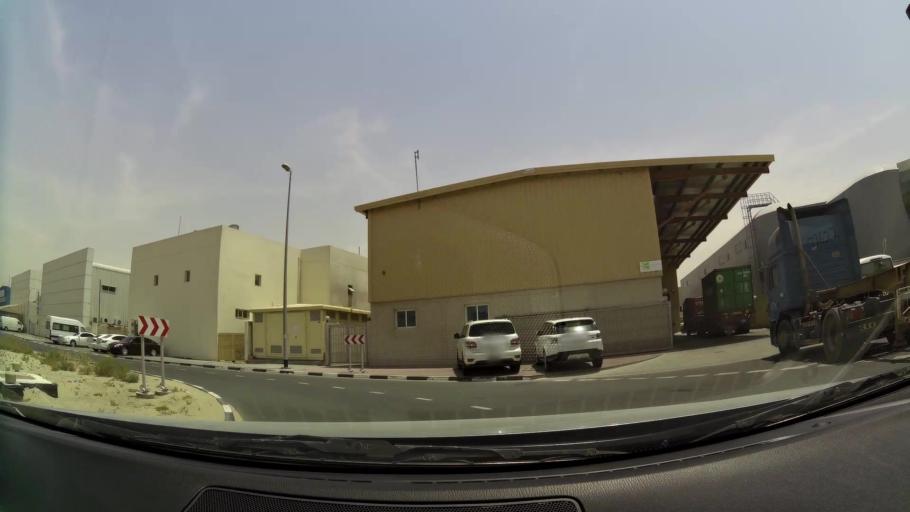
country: AE
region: Ash Shariqah
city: Sharjah
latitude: 25.1868
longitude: 55.3811
